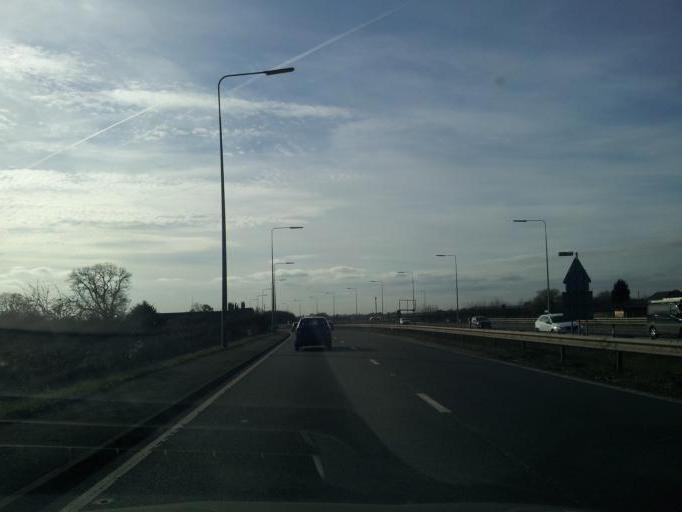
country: GB
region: England
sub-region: Central Bedfordshire
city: Biggleswade
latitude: 52.1019
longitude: -0.2767
